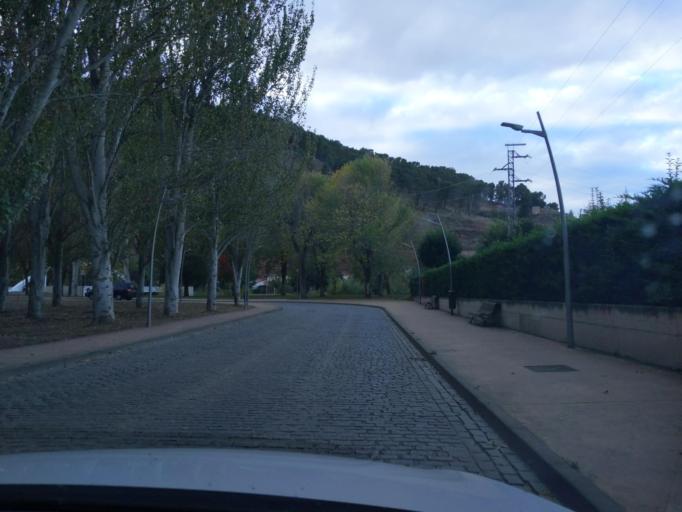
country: ES
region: La Rioja
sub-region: Provincia de La Rioja
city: Najera
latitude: 42.4135
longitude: -2.7322
